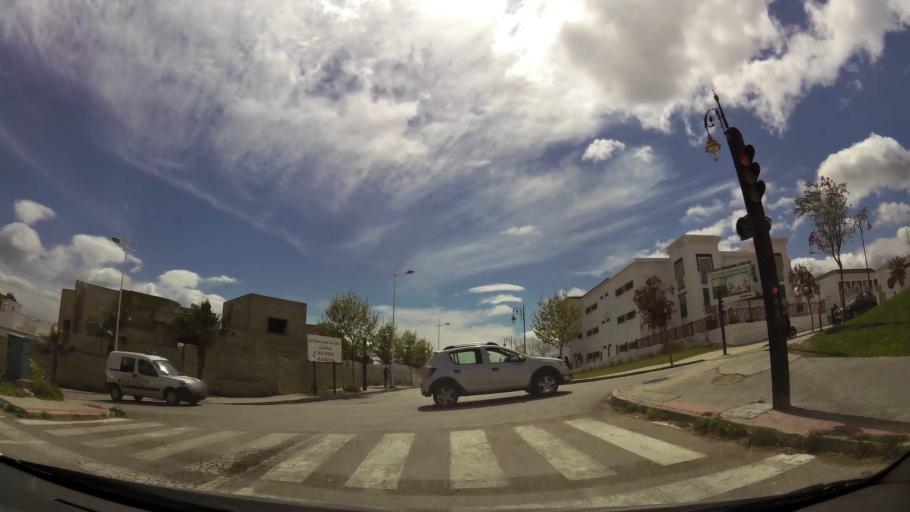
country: MA
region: Tanger-Tetouan
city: Tetouan
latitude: 35.5857
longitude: -5.3386
